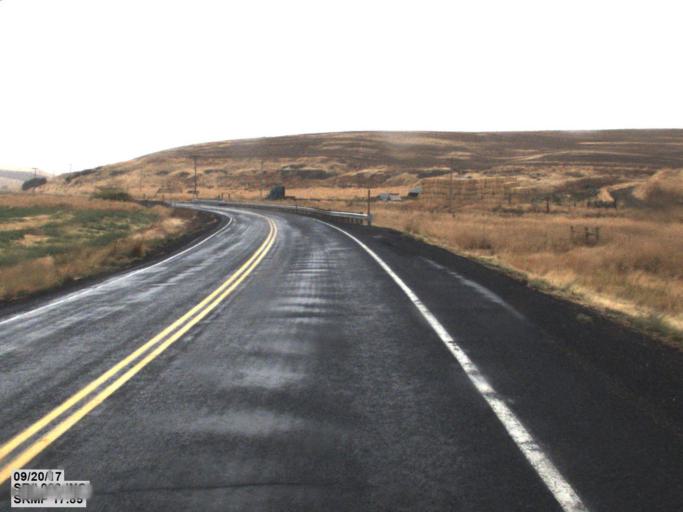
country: US
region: Washington
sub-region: Whitman County
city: Colfax
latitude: 47.1167
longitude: -117.6469
